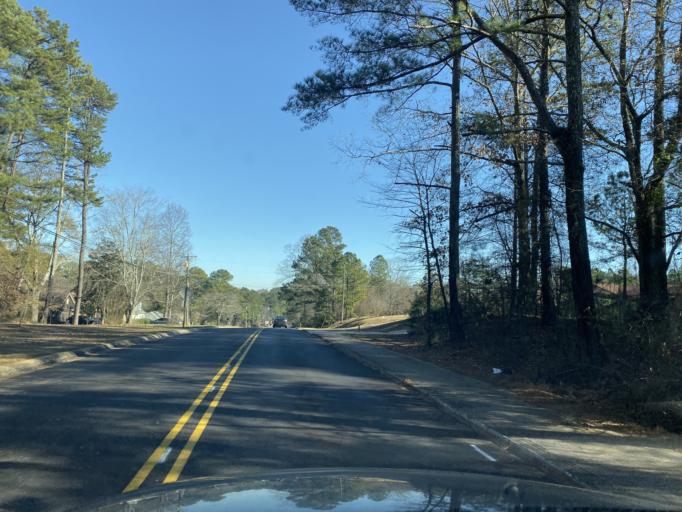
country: US
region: Georgia
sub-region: DeKalb County
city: Pine Mountain
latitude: 33.6765
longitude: -84.1633
